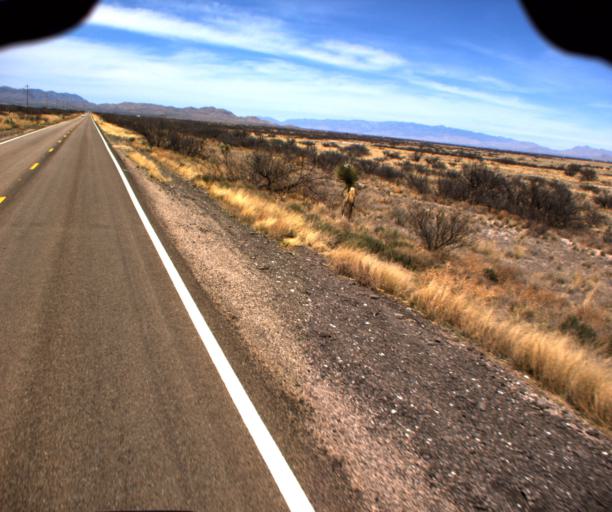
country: US
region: Arizona
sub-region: Cochise County
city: Willcox
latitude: 32.1501
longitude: -109.9360
